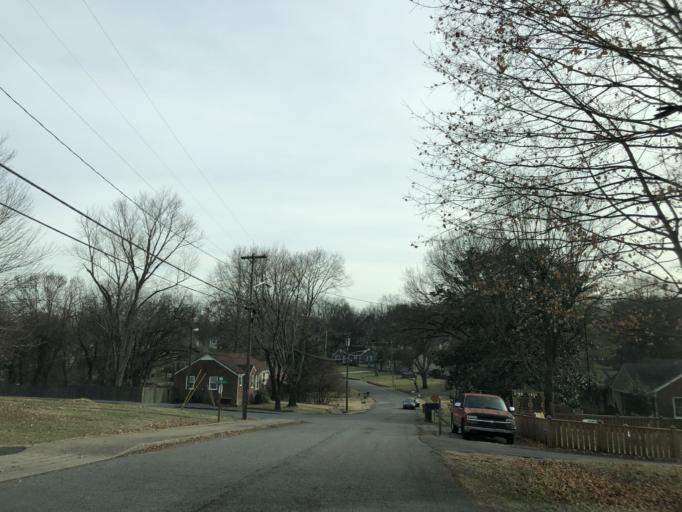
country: US
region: Tennessee
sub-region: Davidson County
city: Nashville
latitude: 36.2047
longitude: -86.7218
